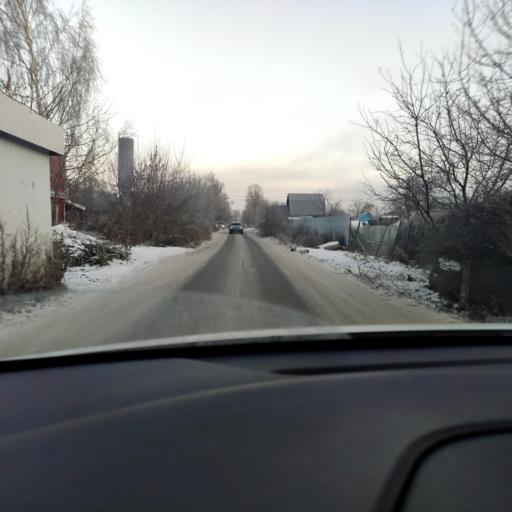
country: RU
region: Tatarstan
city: Staroye Arakchino
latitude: 55.8628
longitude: 49.0467
